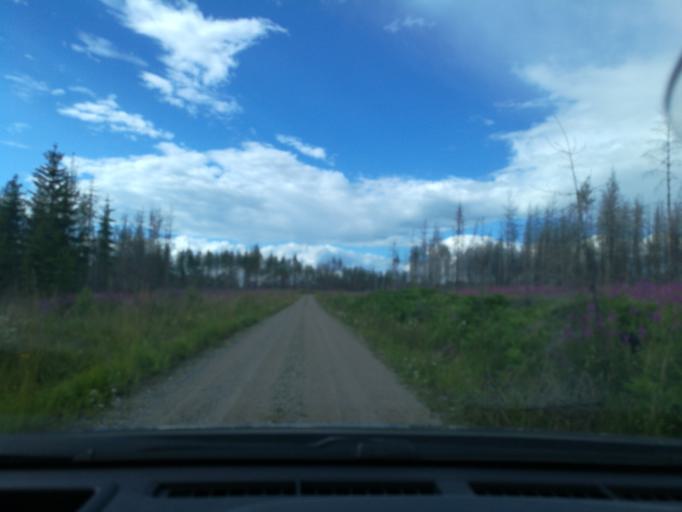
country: SE
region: Vaestmanland
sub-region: Surahammars Kommun
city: Ramnas
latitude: 59.8357
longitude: 16.2421
